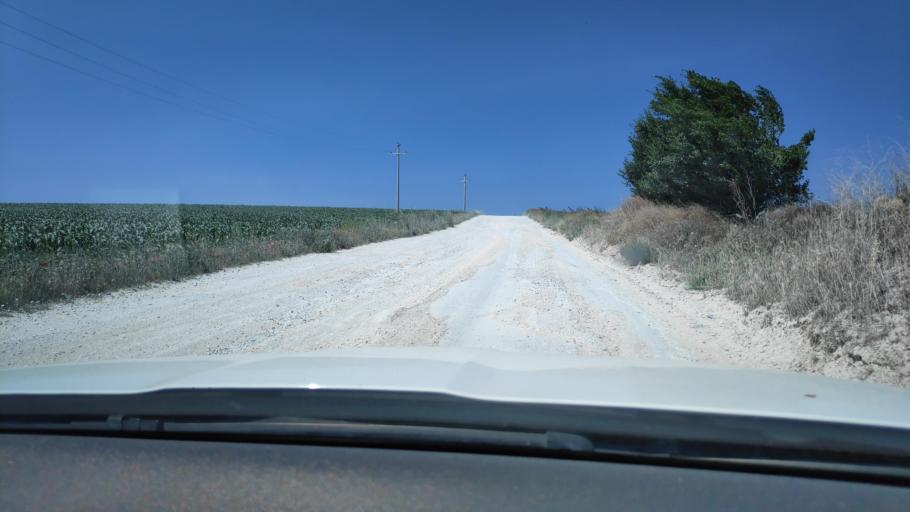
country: MK
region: Kumanovo
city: Romanovce
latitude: 42.0799
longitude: 21.7290
